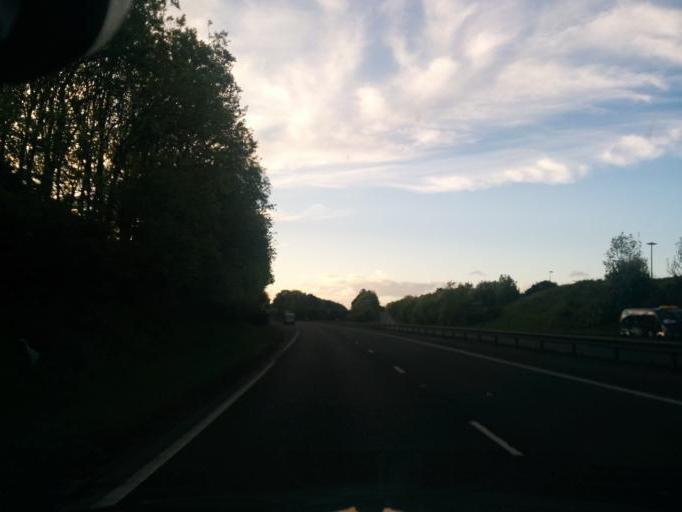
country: GB
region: England
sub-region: Northumberland
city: Bedlington
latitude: 55.1244
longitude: -1.5549
